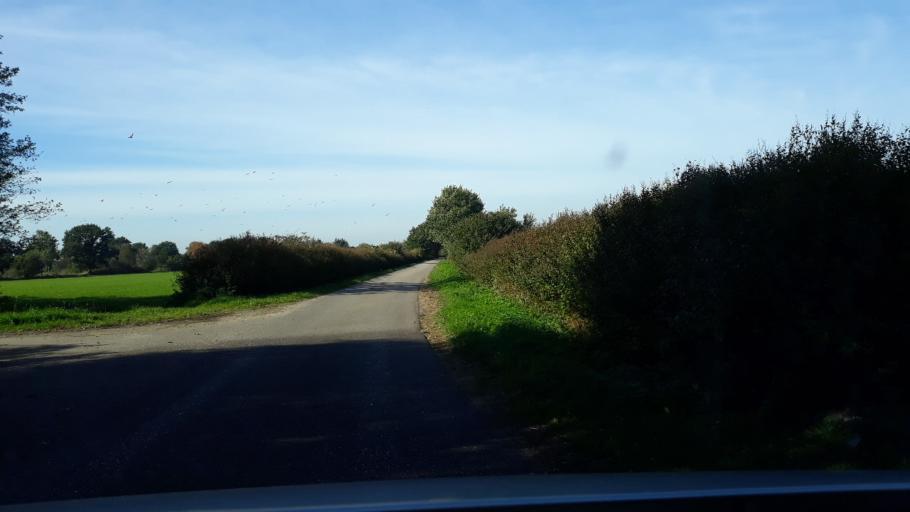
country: DE
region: Schleswig-Holstein
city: Borm
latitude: 54.4226
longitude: 9.4095
